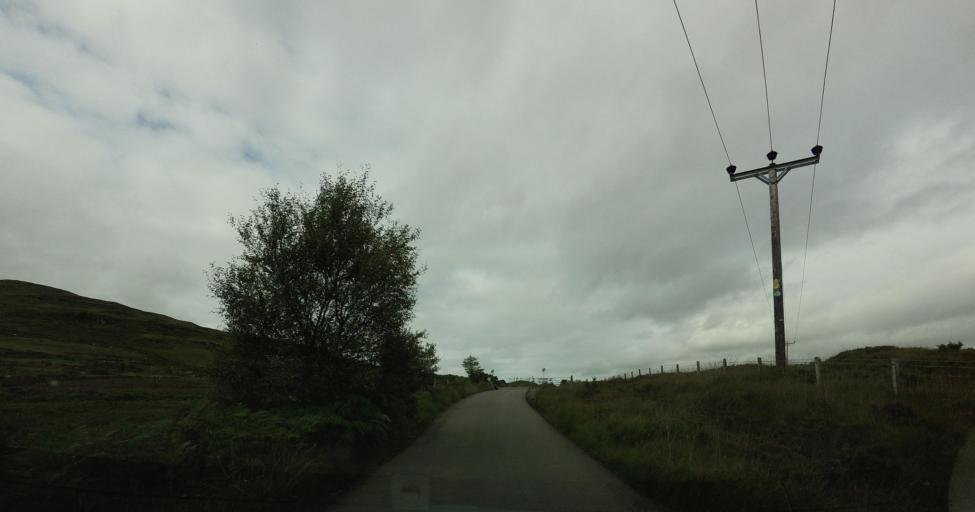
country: GB
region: Scotland
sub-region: Highland
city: Portree
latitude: 57.4138
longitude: -6.2136
